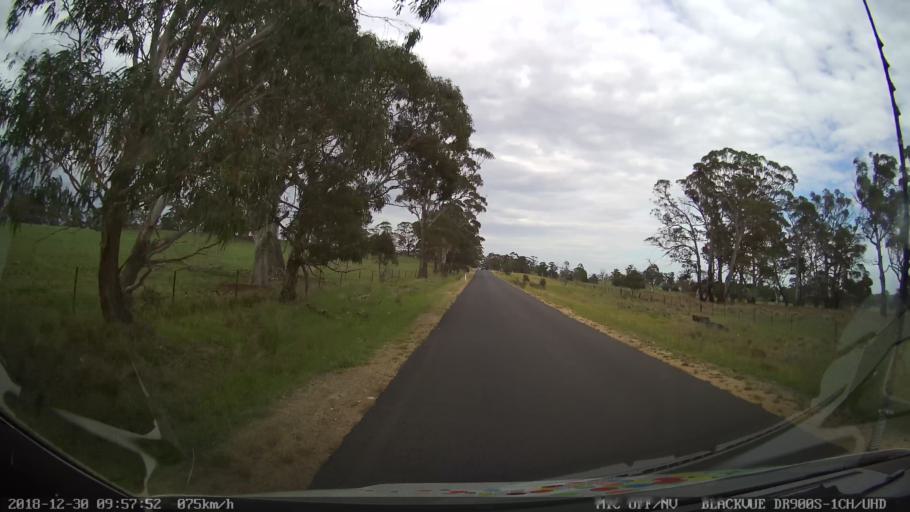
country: AU
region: New South Wales
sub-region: Cooma-Monaro
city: Cooma
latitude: -36.5215
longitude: 149.2339
